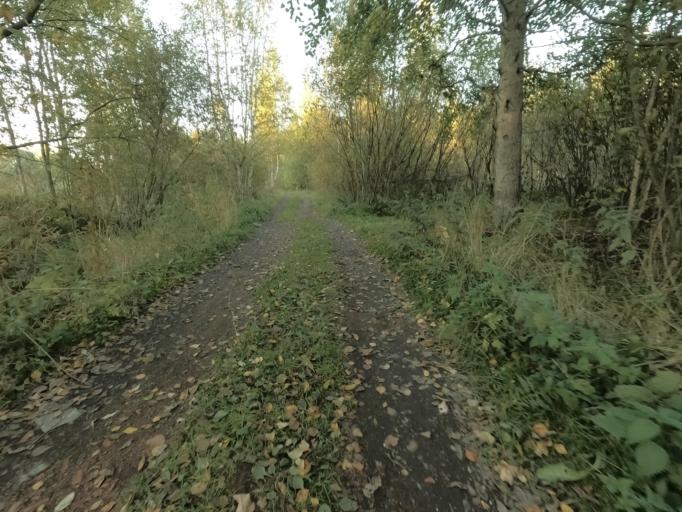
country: RU
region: Leningrad
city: Nikol'skoye
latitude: 59.7132
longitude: 30.7979
